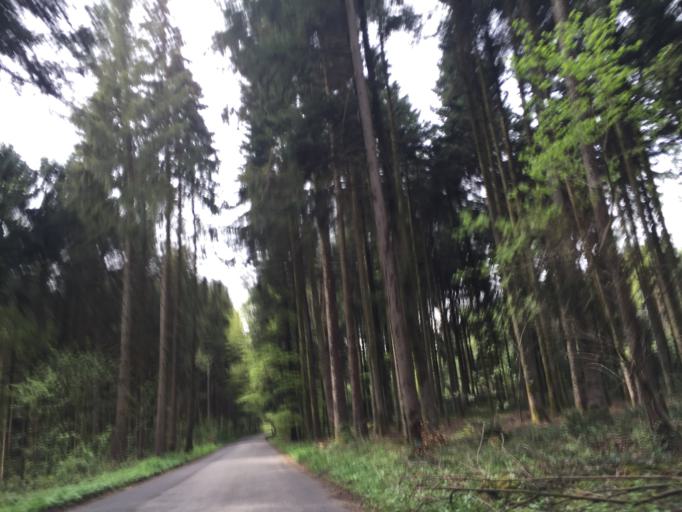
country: CH
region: Bern
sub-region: Bern-Mittelland District
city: Rubigen
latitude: 46.9246
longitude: 7.5353
